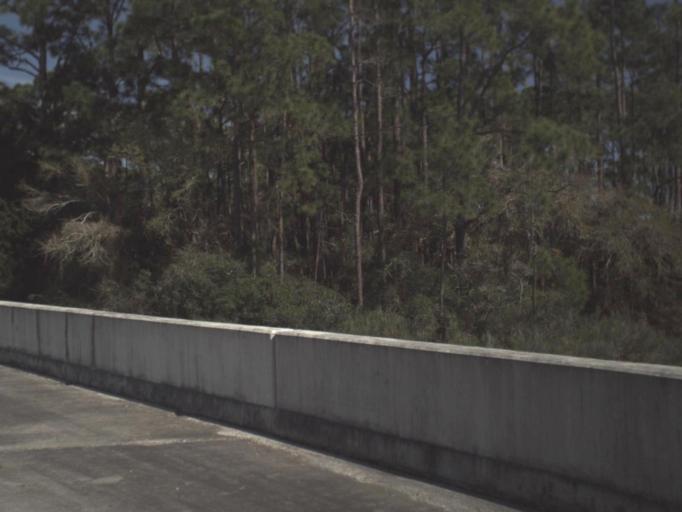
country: US
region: Florida
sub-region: Franklin County
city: Carrabelle
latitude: 29.7896
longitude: -84.7649
